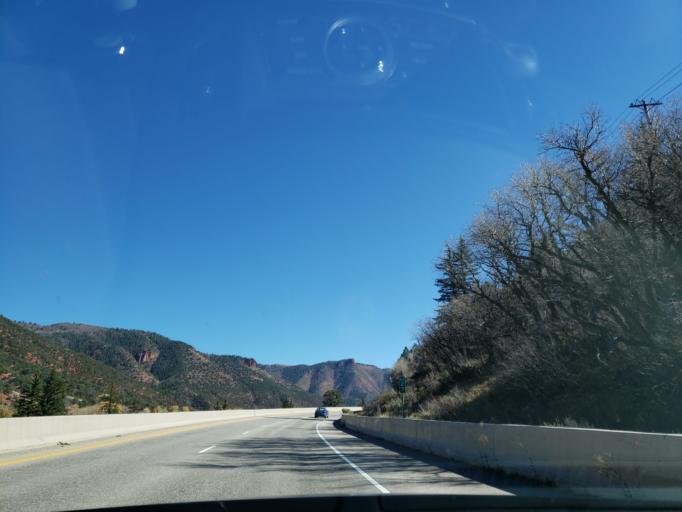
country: US
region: Colorado
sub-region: Eagle County
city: Basalt
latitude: 39.3303
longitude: -106.9804
